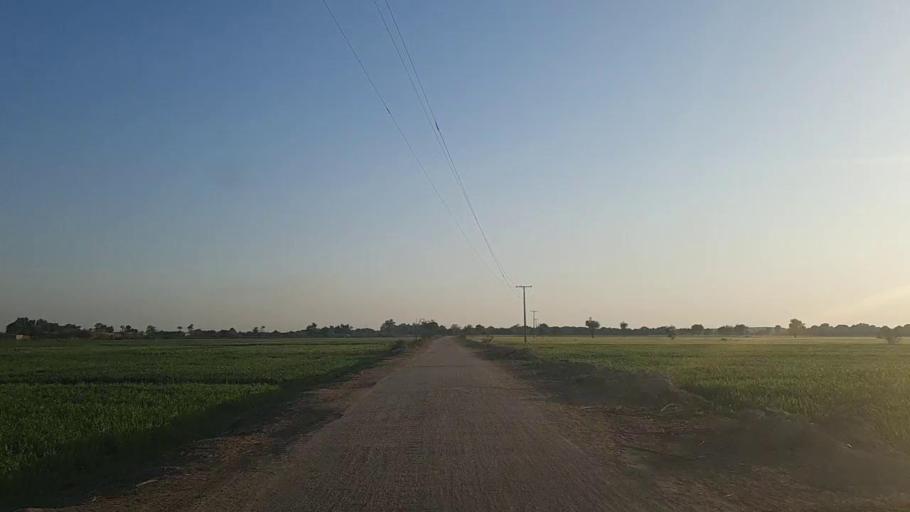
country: PK
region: Sindh
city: Jam Sahib
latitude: 26.3278
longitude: 68.6973
